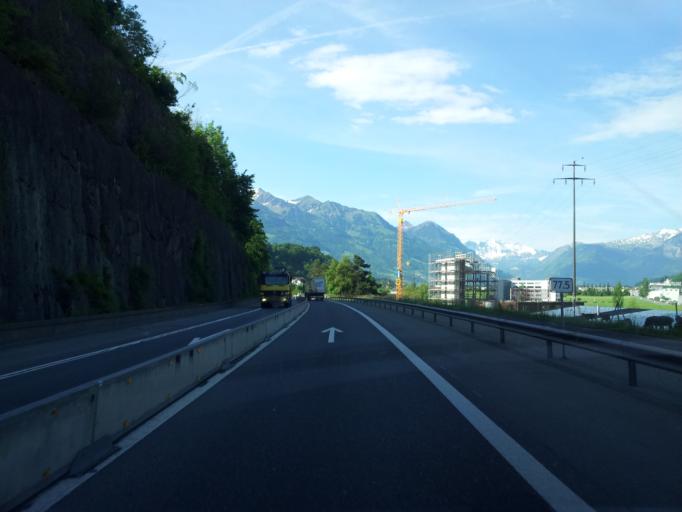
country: CH
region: Obwalden
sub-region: Obwalden
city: Kerns
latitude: 46.9099
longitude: 8.2631
